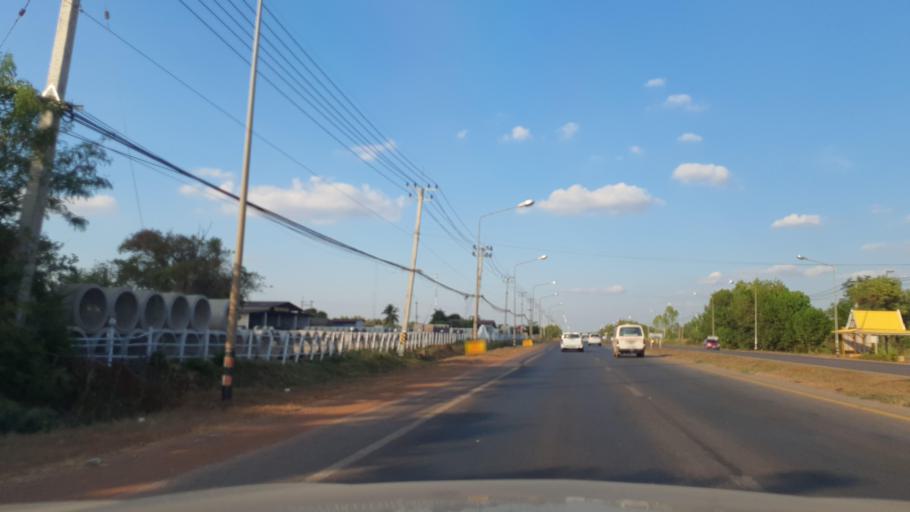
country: TH
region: Sakon Nakhon
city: Sakon Nakhon
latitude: 17.2318
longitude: 104.1076
